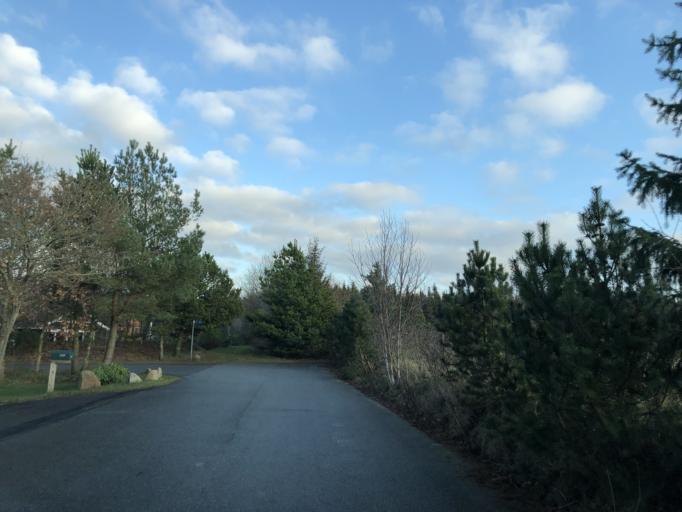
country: DK
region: Central Jutland
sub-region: Holstebro Kommune
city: Ulfborg
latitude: 56.3189
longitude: 8.4366
